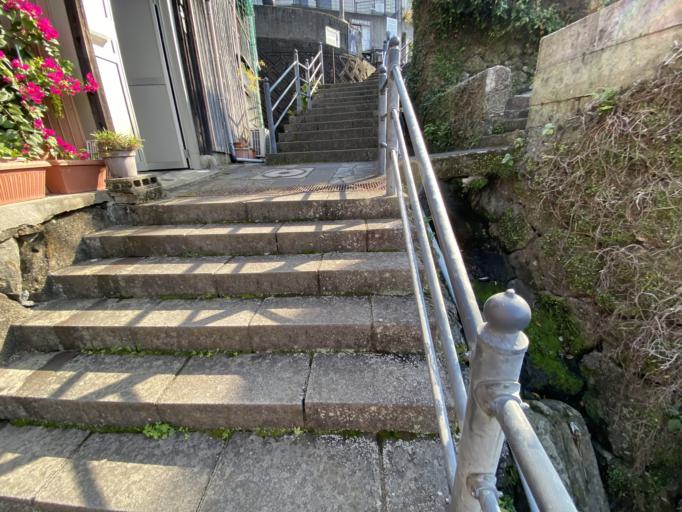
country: JP
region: Nagasaki
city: Nagasaki-shi
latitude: 32.7491
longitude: 129.8863
